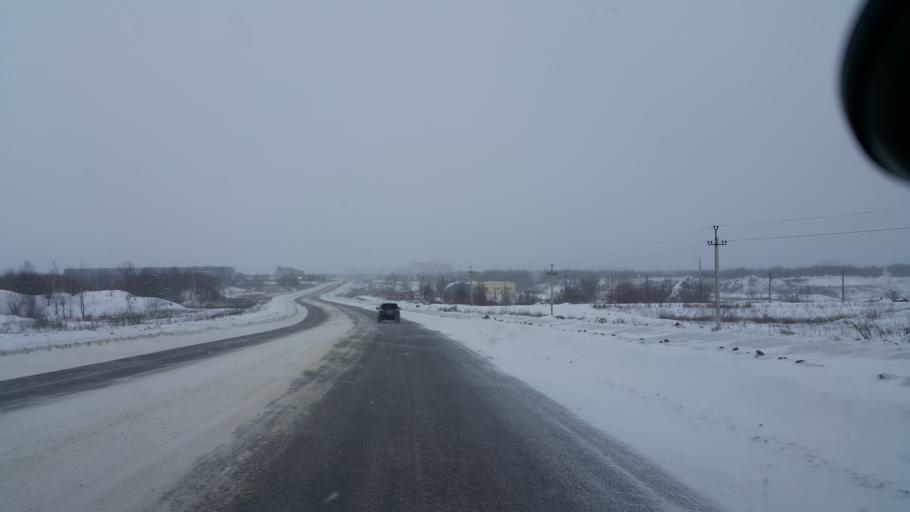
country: RU
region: Tambov
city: Tambov
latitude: 52.7404
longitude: 41.3787
